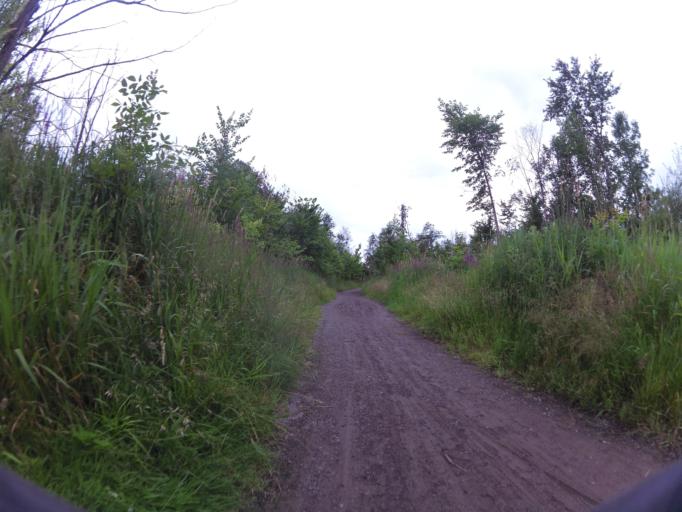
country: CA
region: Ontario
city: Bells Corners
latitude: 45.2476
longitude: -75.7081
